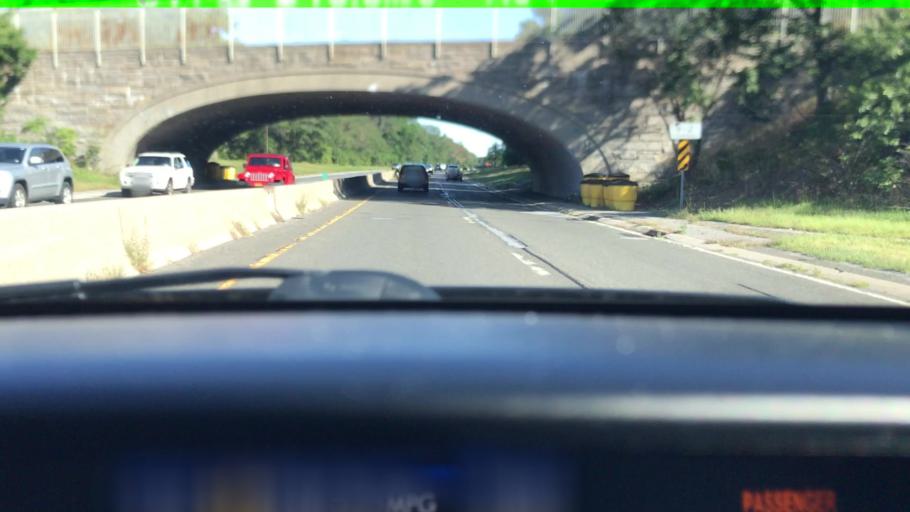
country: US
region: New York
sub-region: Nassau County
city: Salisbury
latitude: 40.7333
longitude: -73.5427
